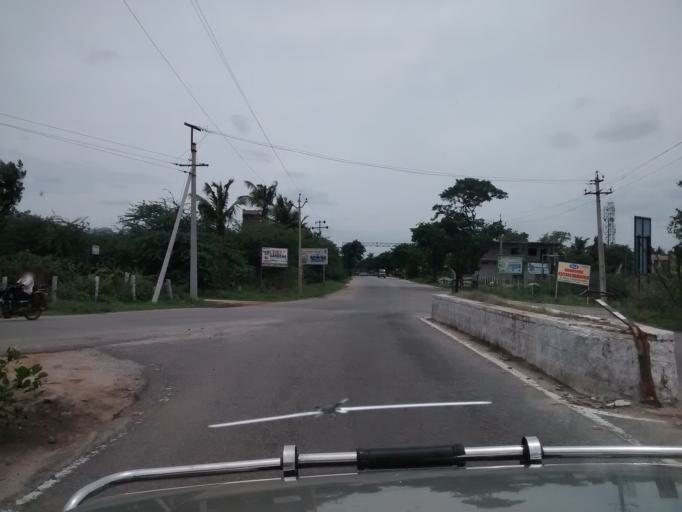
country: IN
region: Andhra Pradesh
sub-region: Chittoor
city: Narasingapuram
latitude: 13.6109
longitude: 79.3327
